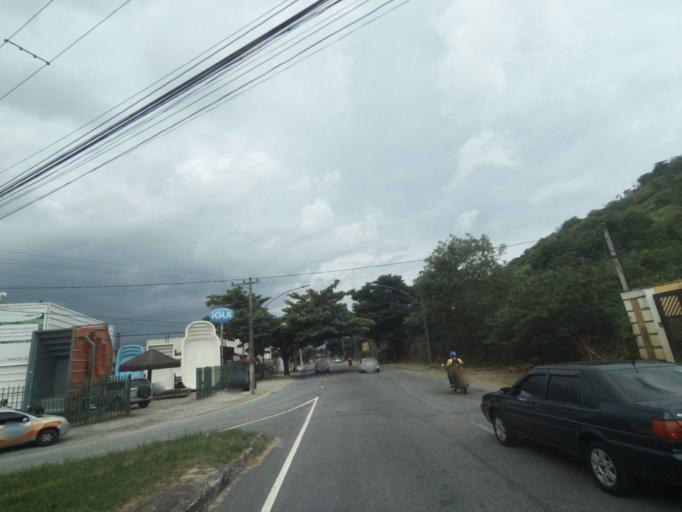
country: BR
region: Rio de Janeiro
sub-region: Nilopolis
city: Nilopolis
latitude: -22.8928
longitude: -43.3947
